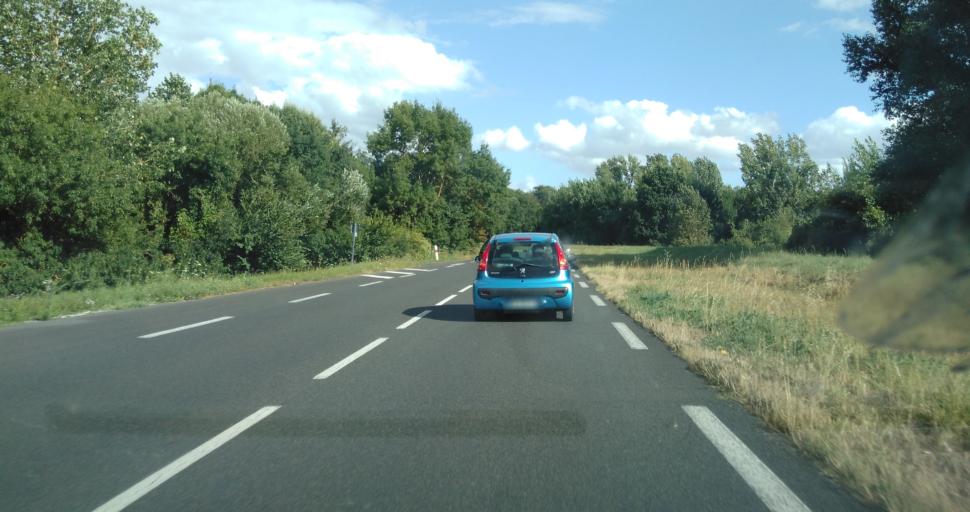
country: FR
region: Centre
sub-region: Departement d'Indre-et-Loire
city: Avoine
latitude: 47.2410
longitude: 0.1716
